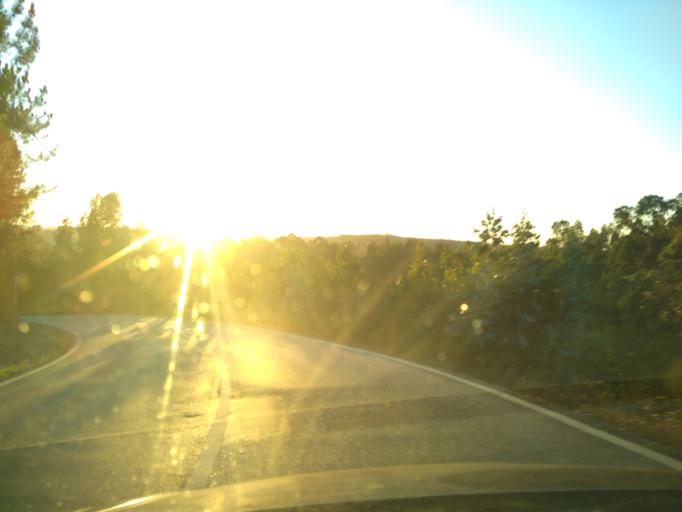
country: PT
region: Coimbra
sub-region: Condeixa-A-Nova
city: Condeixa-a-Nova
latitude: 40.1773
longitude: -8.4801
